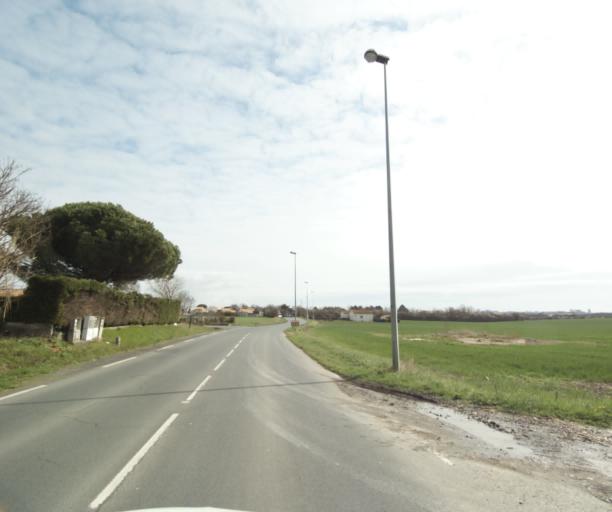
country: FR
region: Poitou-Charentes
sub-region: Departement de la Charente-Maritime
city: Lagord
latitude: 46.1817
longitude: -1.1703
